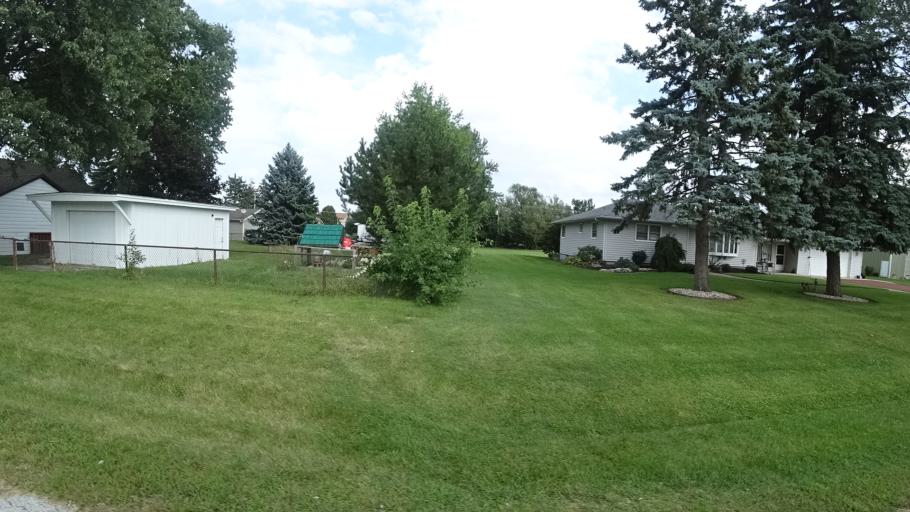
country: US
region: Illinois
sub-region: Cook County
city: Tinley Park
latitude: 41.5581
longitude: -87.7790
